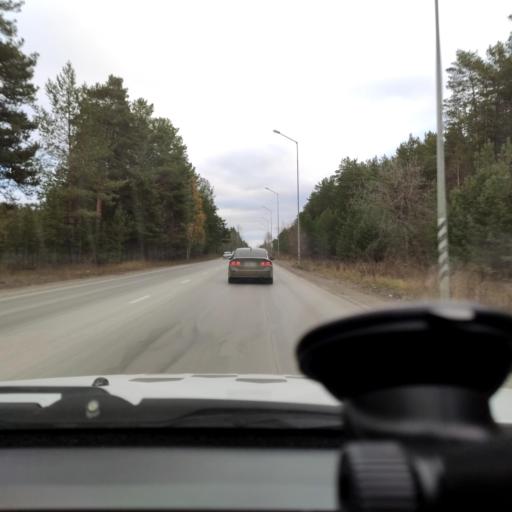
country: RU
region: Perm
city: Perm
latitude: 58.0653
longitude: 56.2715
